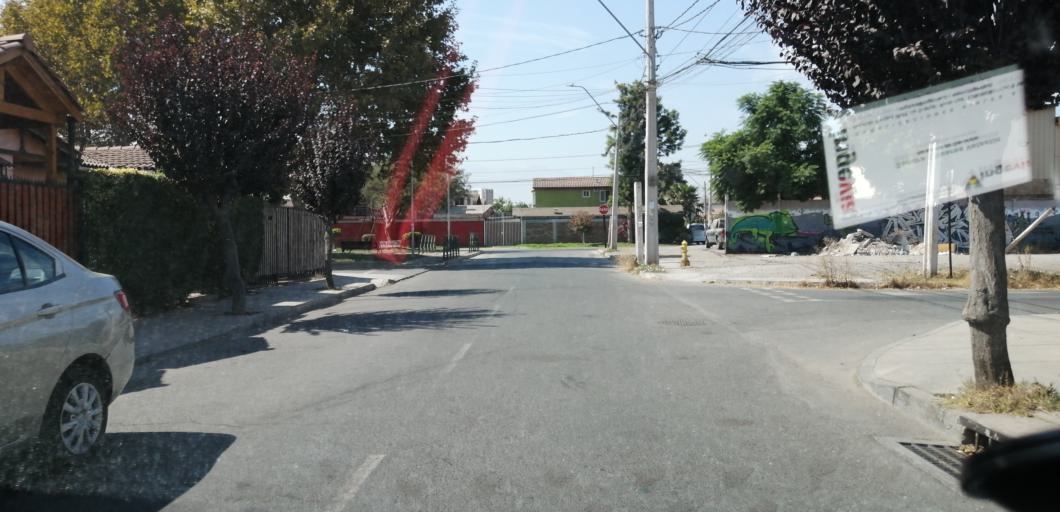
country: CL
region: Santiago Metropolitan
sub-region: Provincia de Santiago
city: Lo Prado
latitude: -33.4538
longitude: -70.7474
